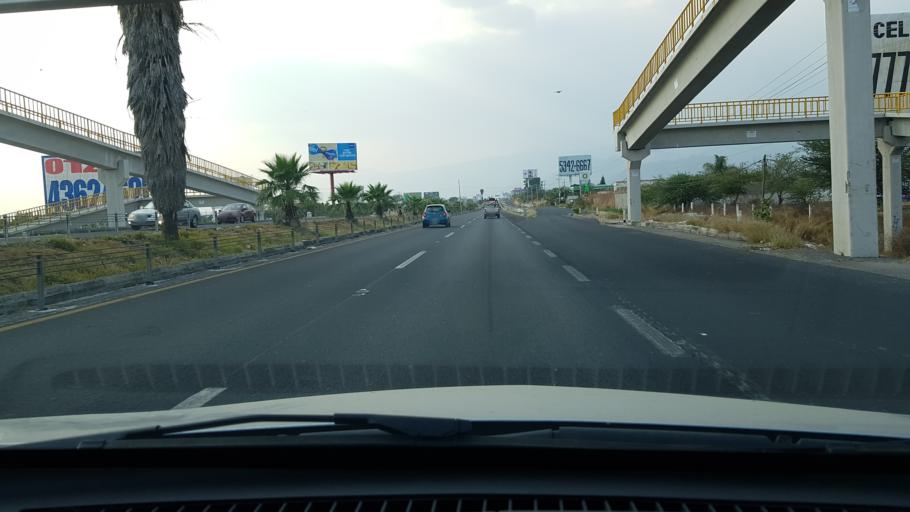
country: MX
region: Morelos
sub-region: Cuautla
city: Tierra Larga (Campo Nuevo)
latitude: 18.8563
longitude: -98.9416
